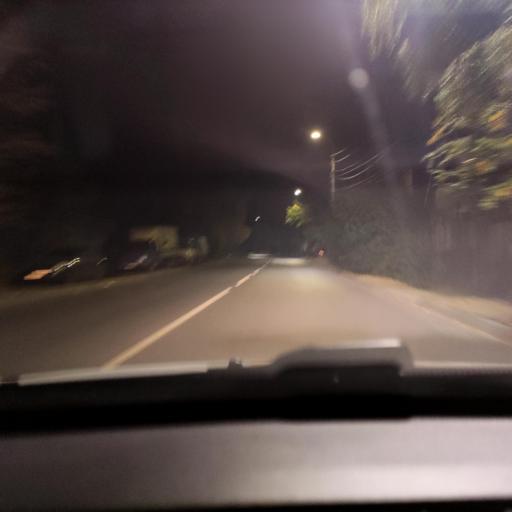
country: RU
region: Voronezj
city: Voronezh
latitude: 51.6825
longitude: 39.2079
